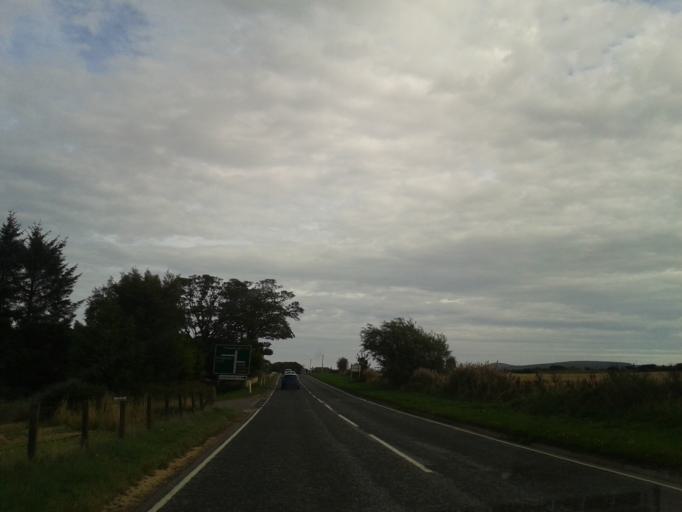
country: GB
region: Scotland
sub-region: Moray
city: Buckie
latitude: 57.6457
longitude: -3.0192
